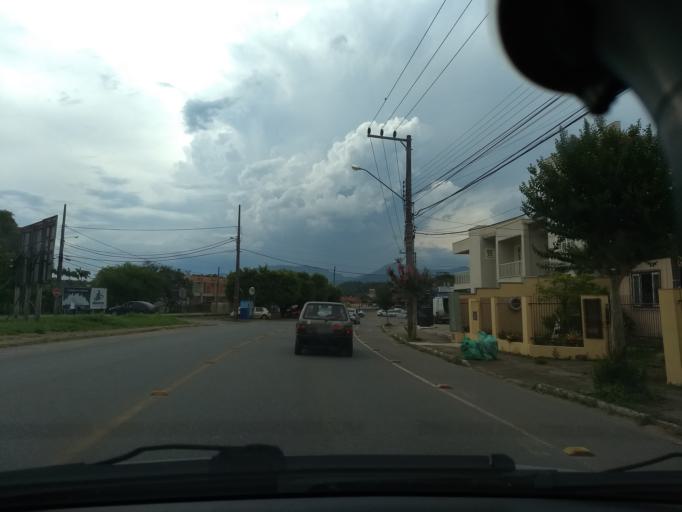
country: BR
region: Santa Catarina
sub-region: Jaragua Do Sul
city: Jaragua do Sul
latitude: -26.4719
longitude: -49.1066
